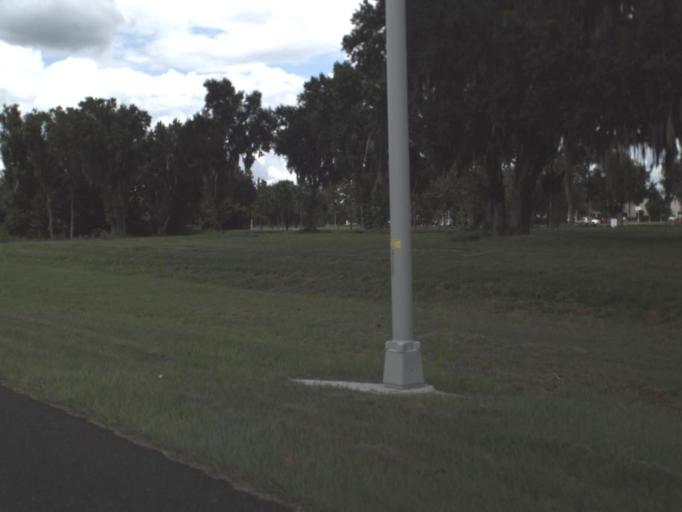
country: US
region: Florida
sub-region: Polk County
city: Bartow
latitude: 27.9159
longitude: -81.8457
